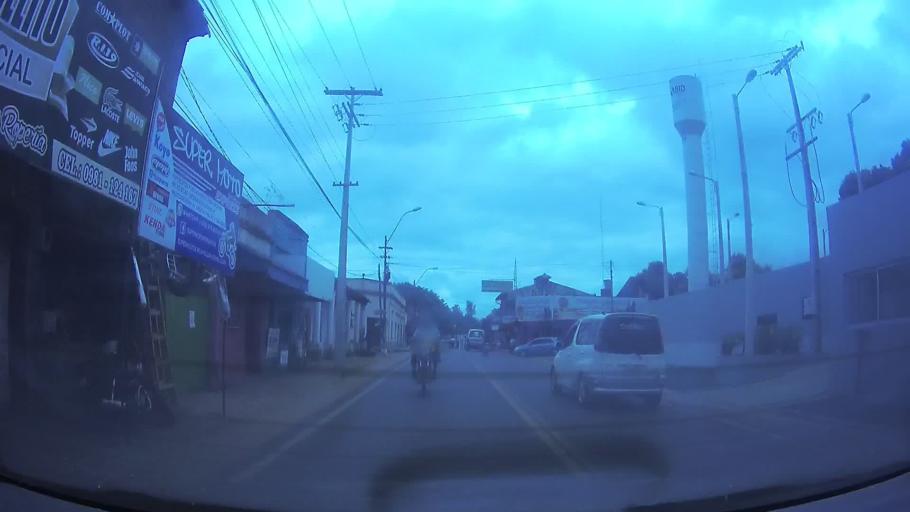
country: PY
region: Paraguari
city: Carapegua
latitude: -25.7687
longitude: -57.2424
